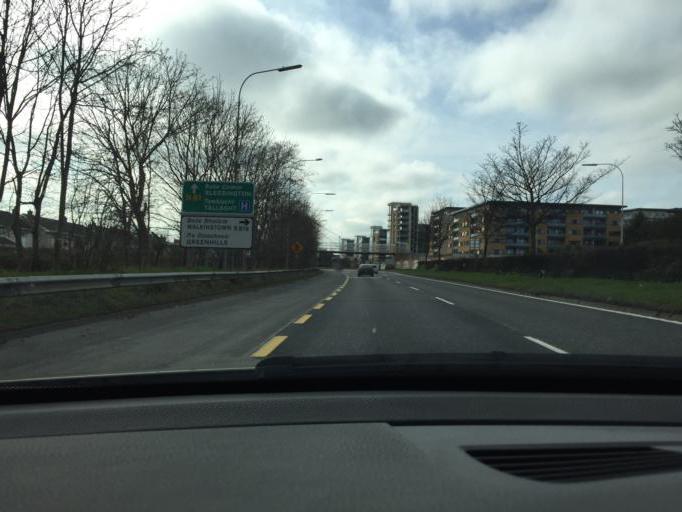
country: IE
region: Leinster
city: Firhouse
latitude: 53.2869
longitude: -6.3532
